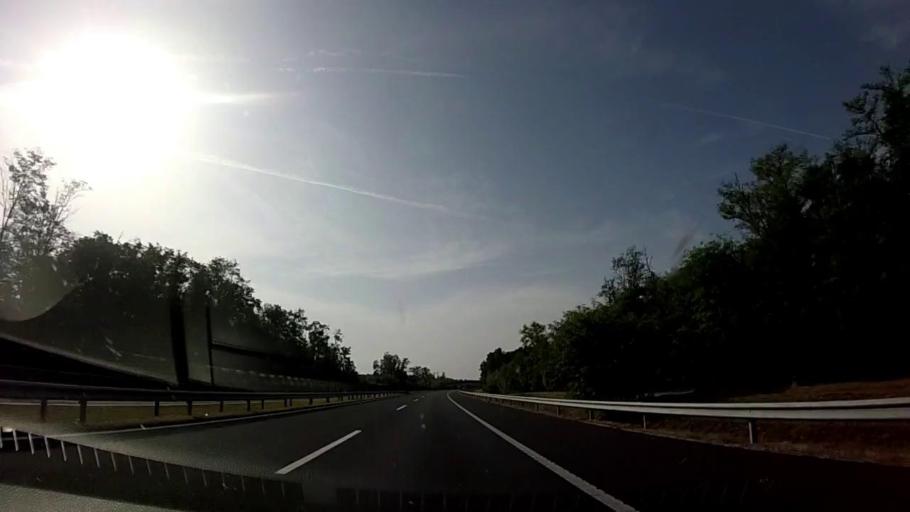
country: HU
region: Zala
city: Zalakomar
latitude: 46.5754
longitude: 17.2487
